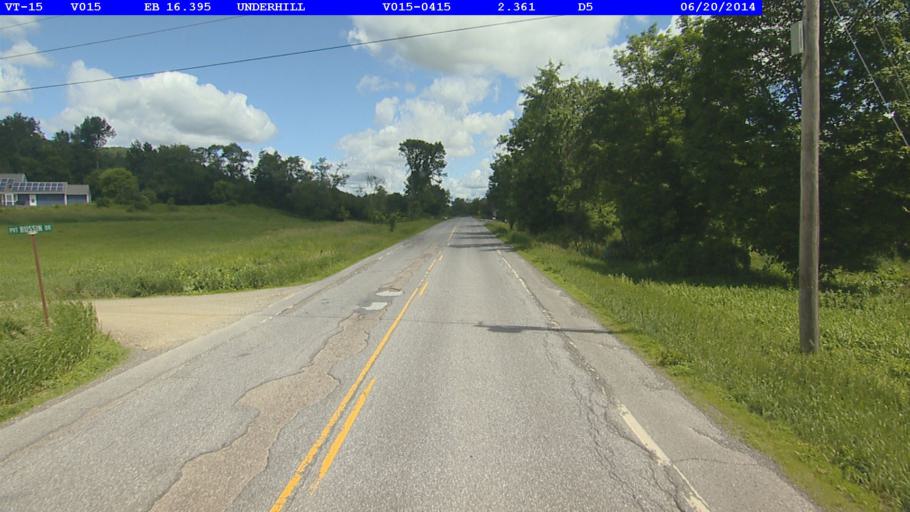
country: US
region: Vermont
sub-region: Chittenden County
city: Jericho
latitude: 44.5579
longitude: -72.9437
